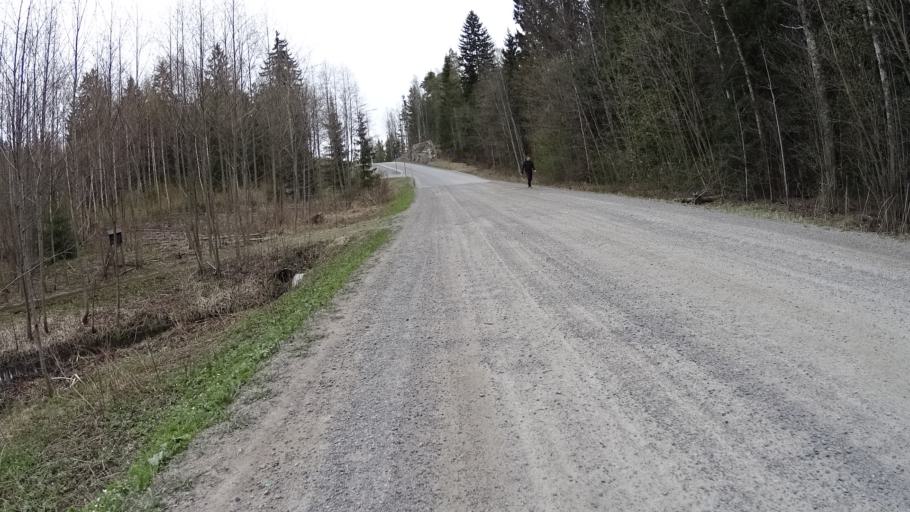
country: FI
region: Uusimaa
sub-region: Helsinki
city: Kilo
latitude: 60.2579
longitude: 24.7913
